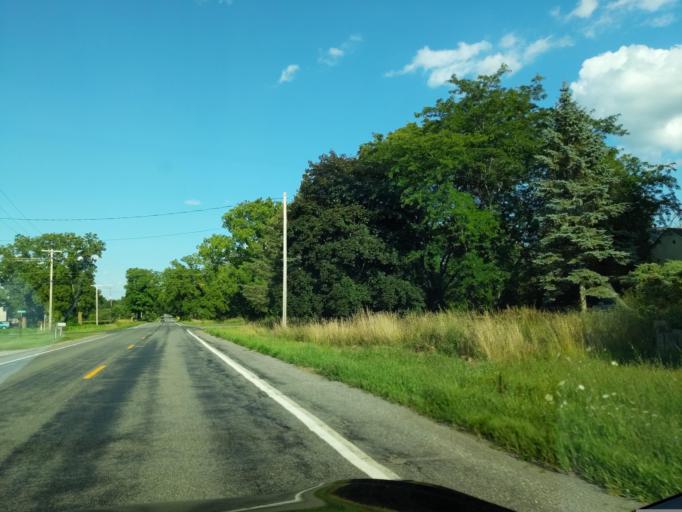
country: US
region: Michigan
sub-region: Ingham County
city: Holt
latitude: 42.5821
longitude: -84.5437
